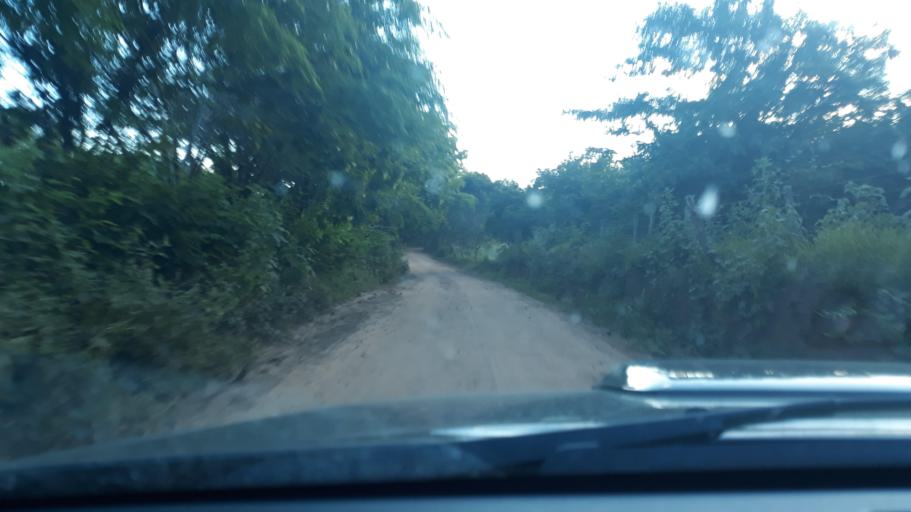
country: BR
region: Bahia
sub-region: Riacho De Santana
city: Riacho de Santana
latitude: -13.8118
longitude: -42.7204
